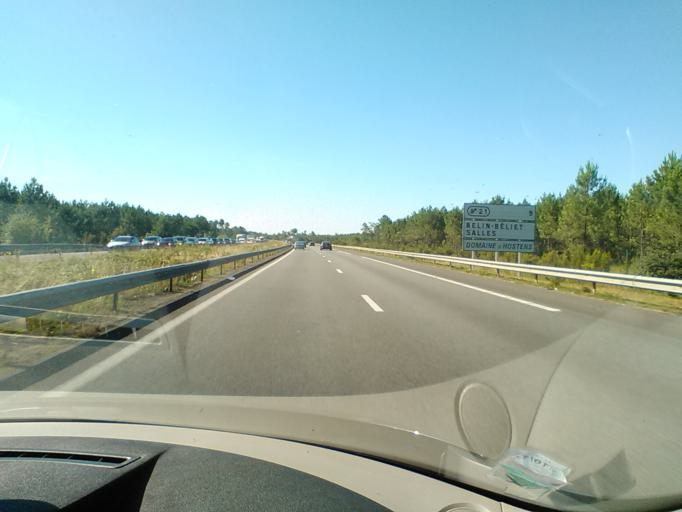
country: FR
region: Aquitaine
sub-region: Departement de la Gironde
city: Salles
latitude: 44.6156
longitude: -0.8507
